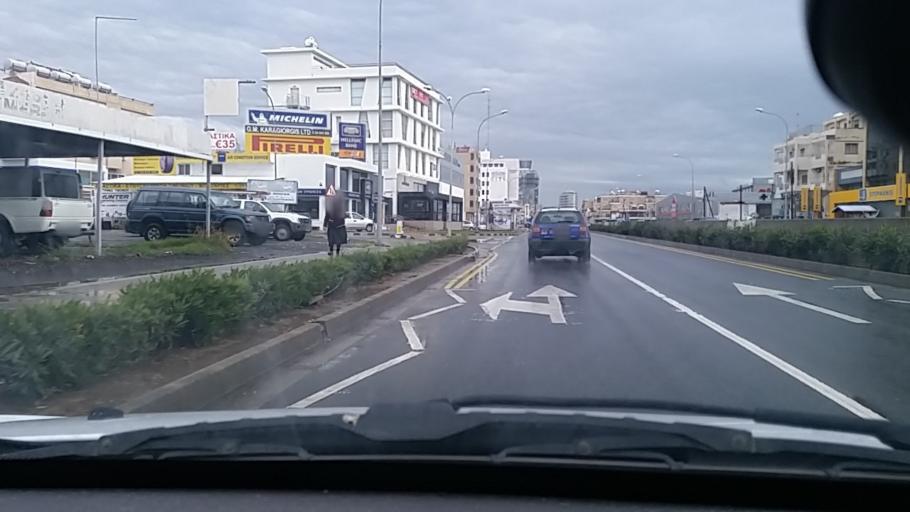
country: CY
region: Larnaka
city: Larnaca
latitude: 34.9301
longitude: 33.6205
